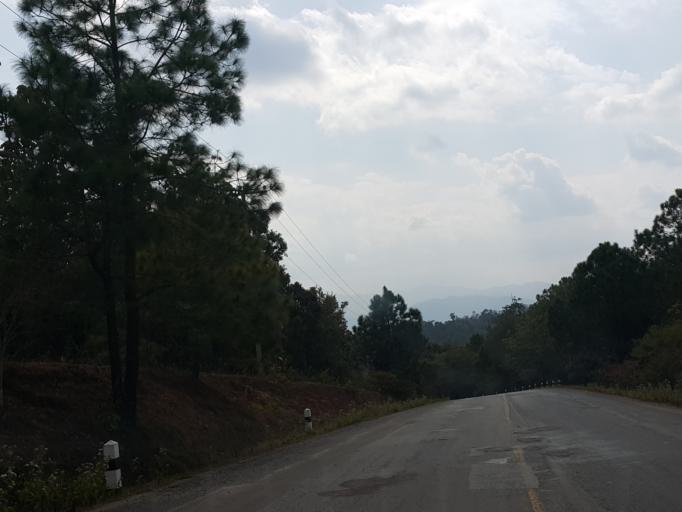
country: TH
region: Chiang Mai
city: Om Koi
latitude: 17.8588
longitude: 98.3731
